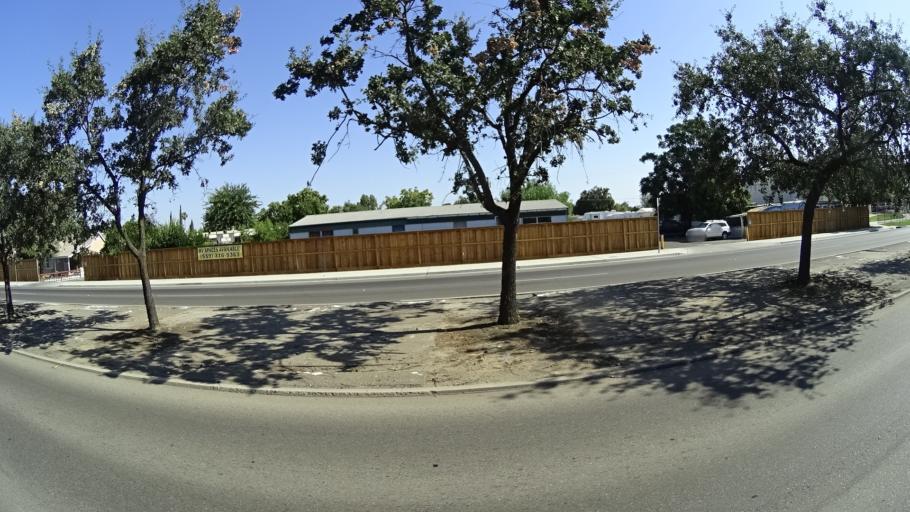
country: US
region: California
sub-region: Fresno County
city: Fresno
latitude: 36.7068
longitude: -119.7473
